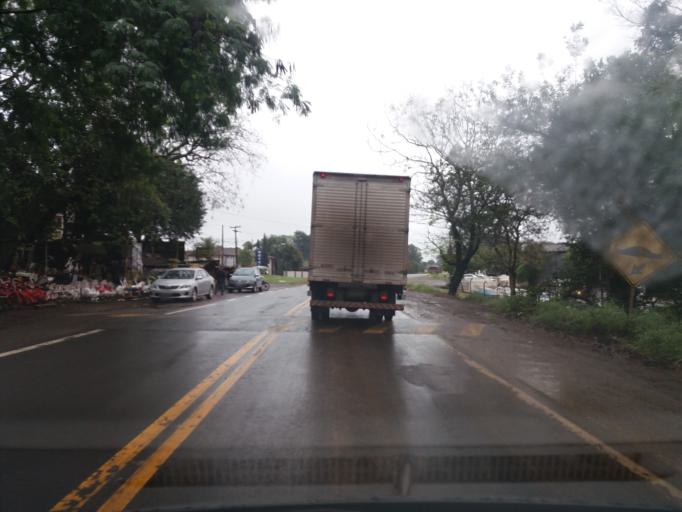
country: BR
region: Parana
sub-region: Realeza
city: Realeza
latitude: -25.4929
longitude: -53.5982
